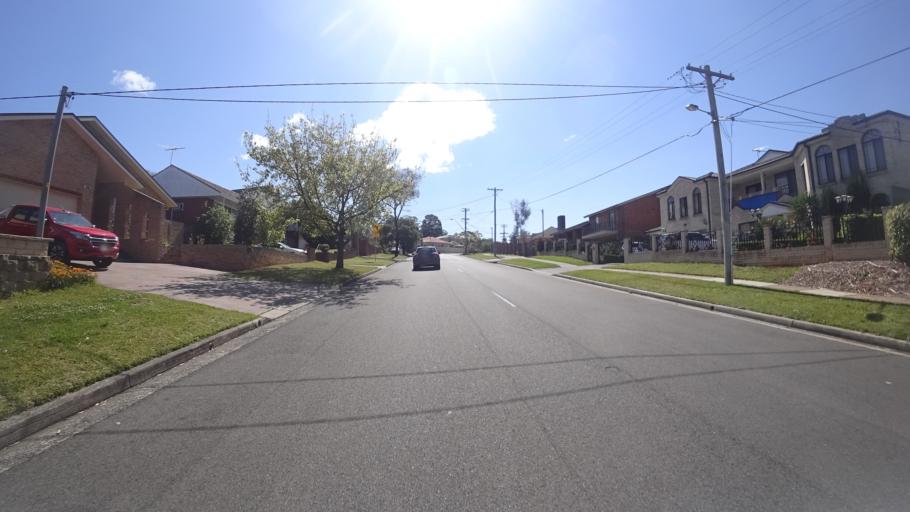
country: AU
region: New South Wales
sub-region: Fairfield
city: Cabramatta West
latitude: -33.9094
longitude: 150.9044
